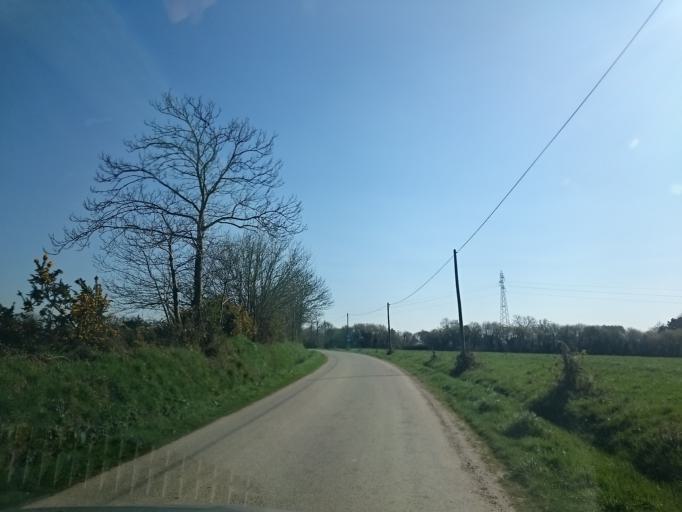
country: FR
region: Brittany
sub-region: Departement d'Ille-et-Vilaine
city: Crevin
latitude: 47.9658
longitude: -1.6780
